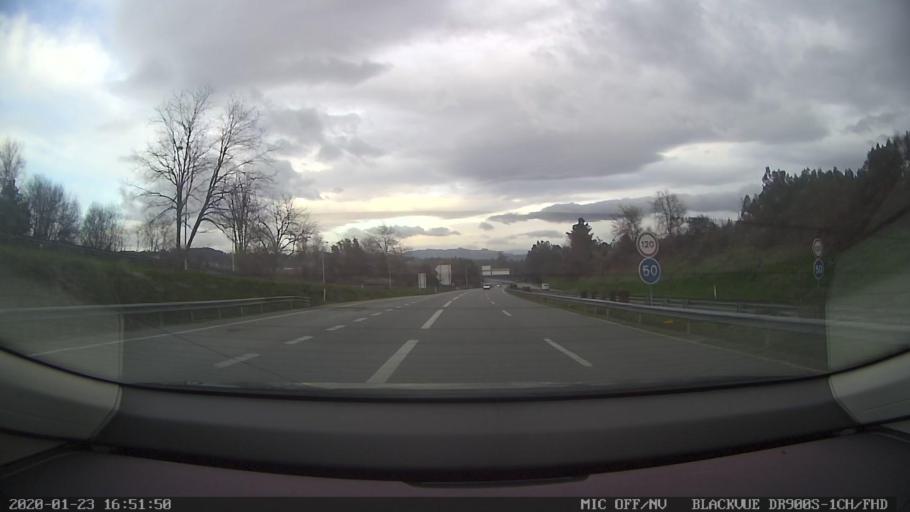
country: PT
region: Porto
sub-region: Lousada
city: Meinedo
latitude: 41.2326
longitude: -8.2099
